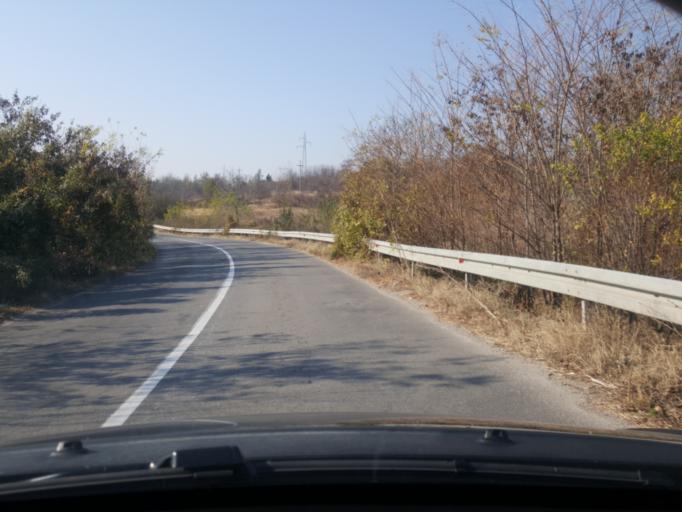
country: RS
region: Central Serbia
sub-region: Nisavski Okrug
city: Niska Banja
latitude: 43.3196
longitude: 22.0030
